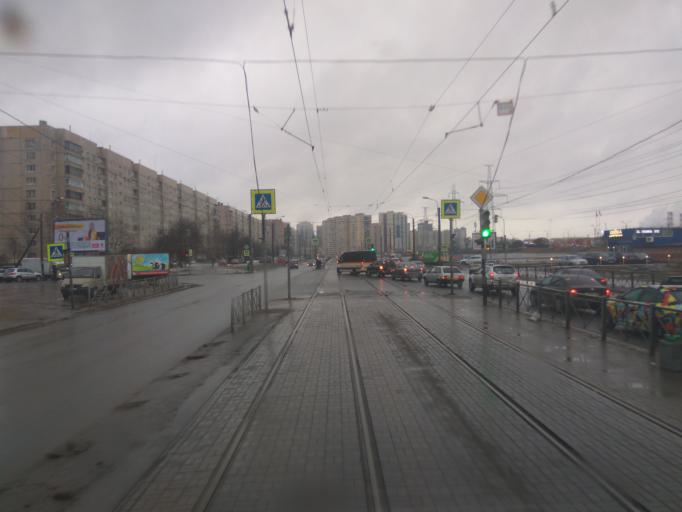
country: RU
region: St.-Petersburg
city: Dachnoye
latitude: 59.8600
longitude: 30.2149
